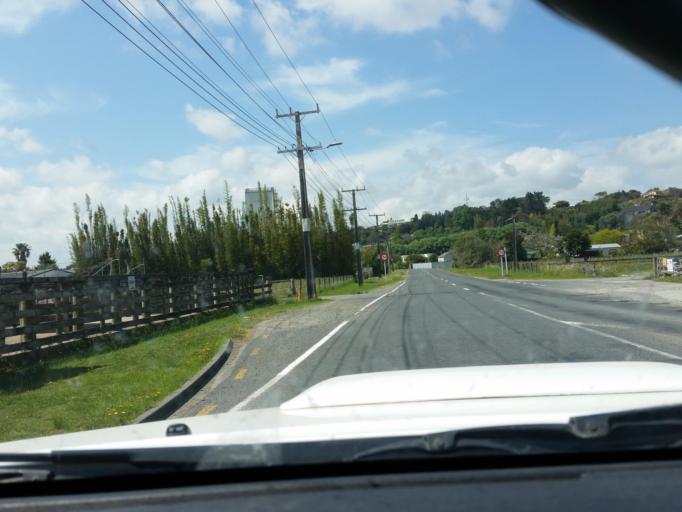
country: NZ
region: Northland
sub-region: Kaipara District
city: Dargaville
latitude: -35.9512
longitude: 173.8629
